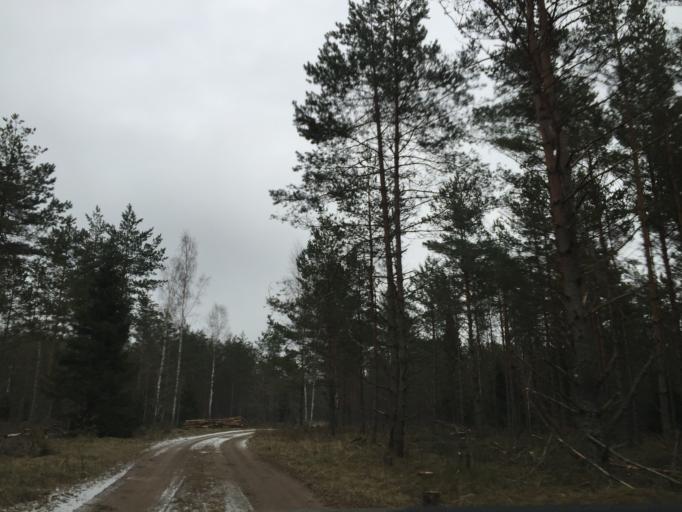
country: EE
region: Saare
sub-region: Kuressaare linn
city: Kuressaare
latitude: 58.3879
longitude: 22.2569
